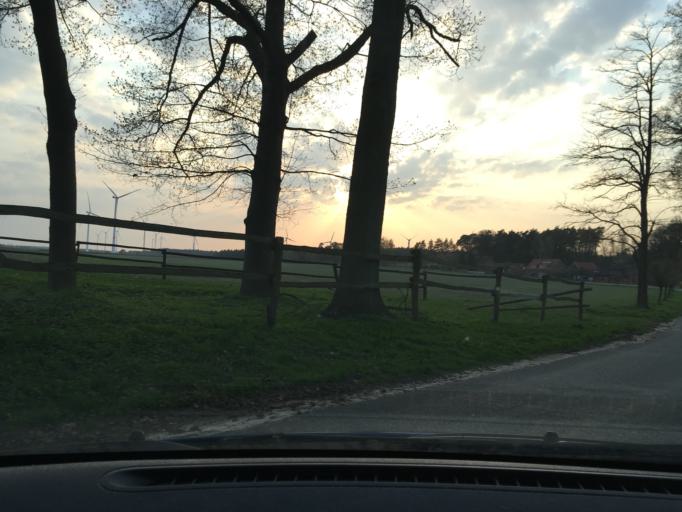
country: DE
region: Lower Saxony
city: Embsen
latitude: 53.1945
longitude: 10.3232
